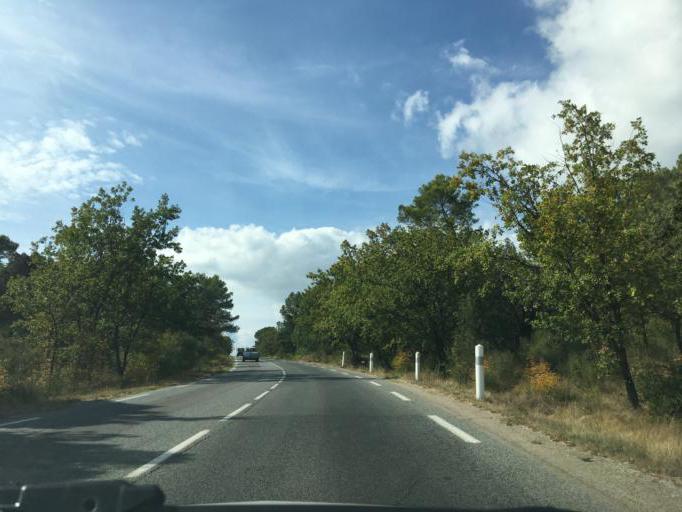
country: FR
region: Provence-Alpes-Cote d'Azur
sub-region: Departement du Var
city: Flayosc
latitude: 43.5446
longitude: 6.3440
